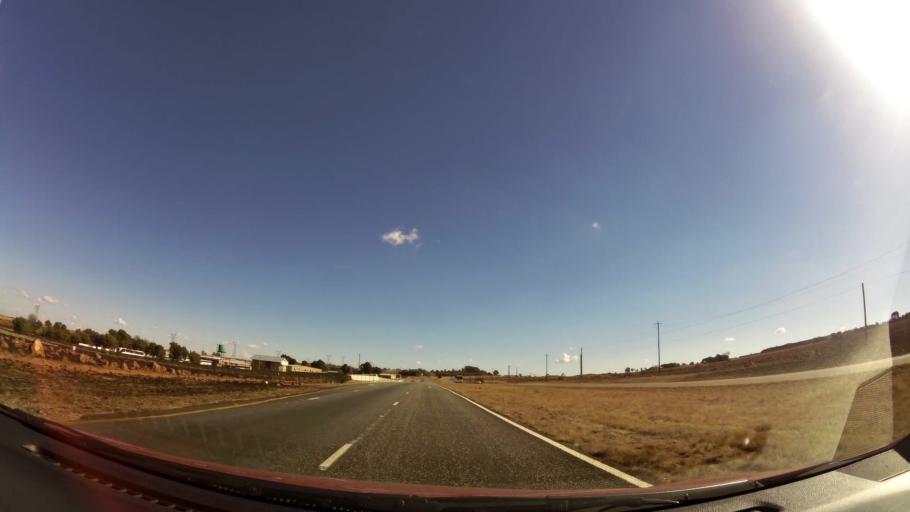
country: ZA
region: Gauteng
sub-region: West Rand District Municipality
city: Carletonville
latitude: -26.4162
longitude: 27.4486
